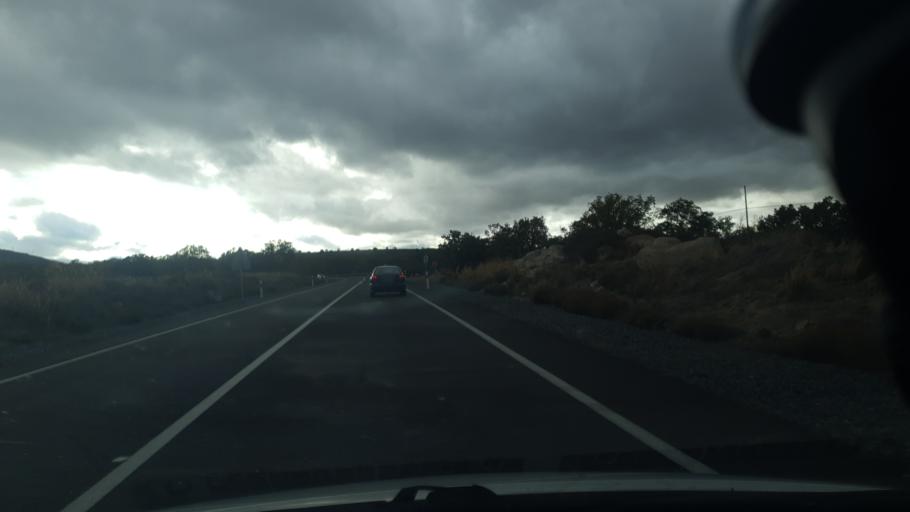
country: ES
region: Castille and Leon
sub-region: Provincia de Segovia
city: Villacastin
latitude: 40.7583
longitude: -4.4423
